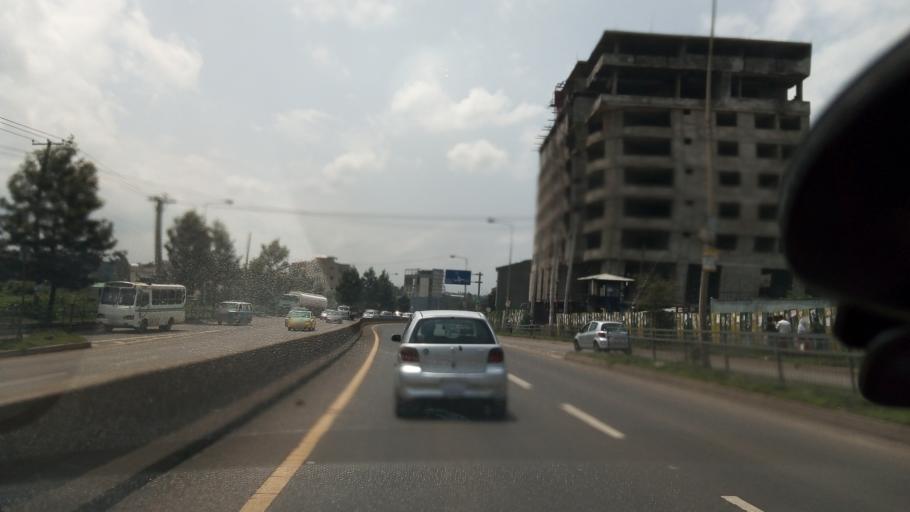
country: ET
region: Adis Abeba
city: Addis Ababa
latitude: 8.9646
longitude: 38.7308
